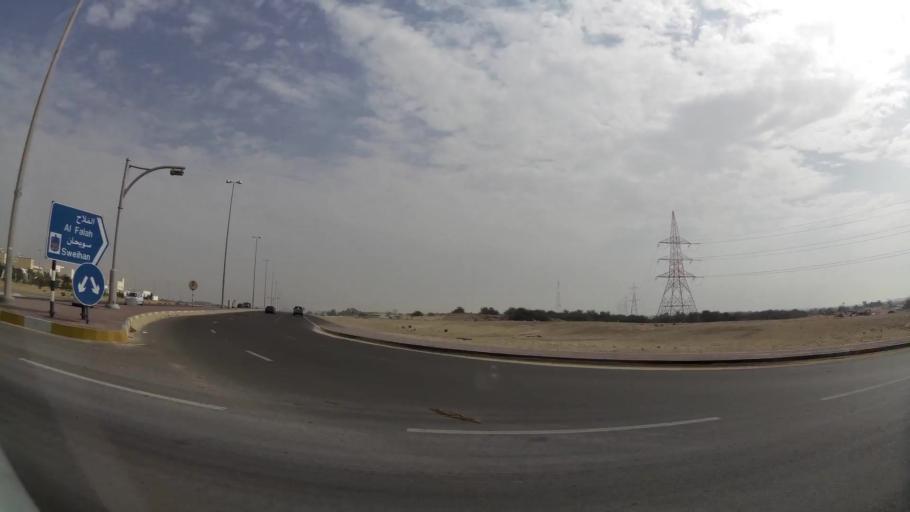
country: AE
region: Abu Dhabi
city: Abu Dhabi
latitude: 24.2963
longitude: 54.6619
